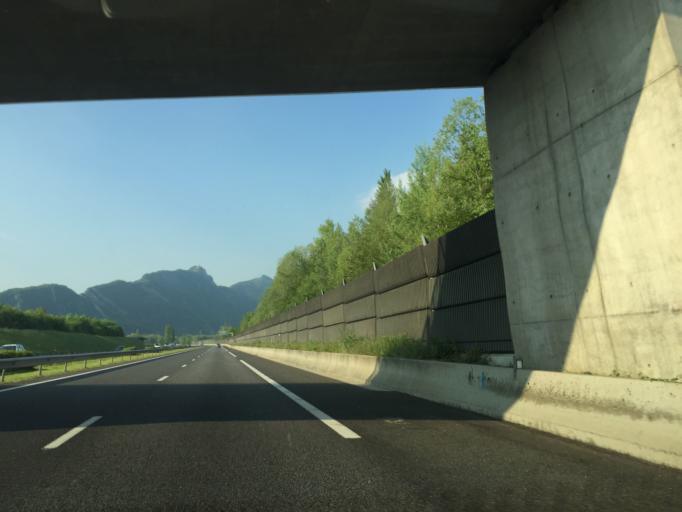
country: FR
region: Rhone-Alpes
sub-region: Departement de l'Isere
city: Allieres-et-Risset
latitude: 45.0938
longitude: 5.6701
